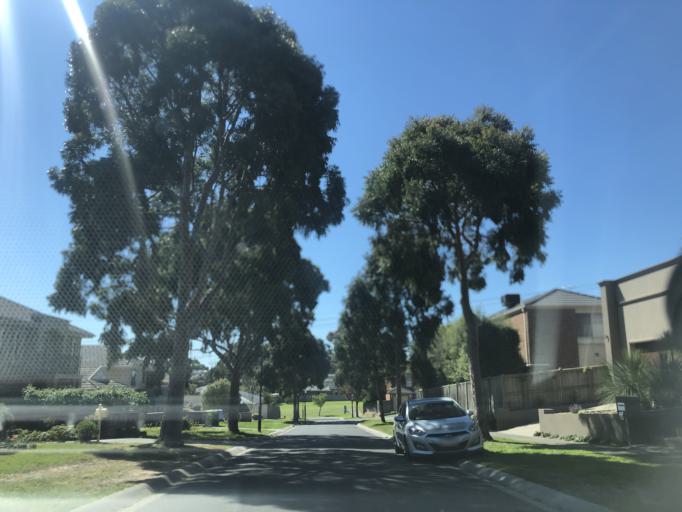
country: AU
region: Victoria
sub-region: Monash
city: Notting Hill
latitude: -37.8929
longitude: 145.1381
